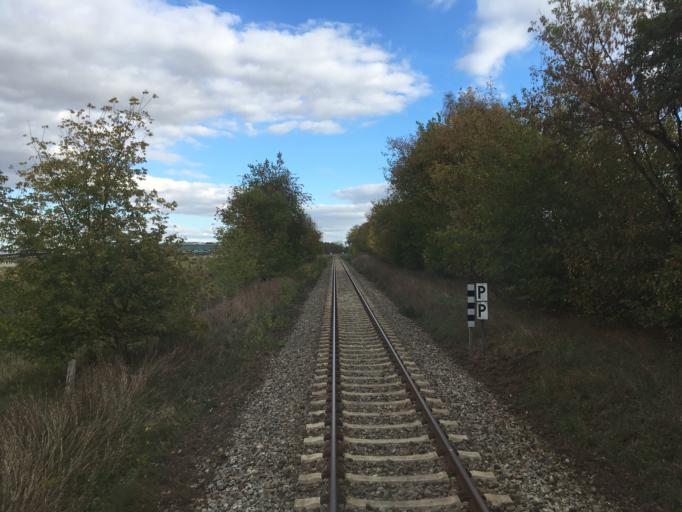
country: DE
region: Mecklenburg-Vorpommern
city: Grabowhofe
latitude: 53.5402
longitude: 12.5984
